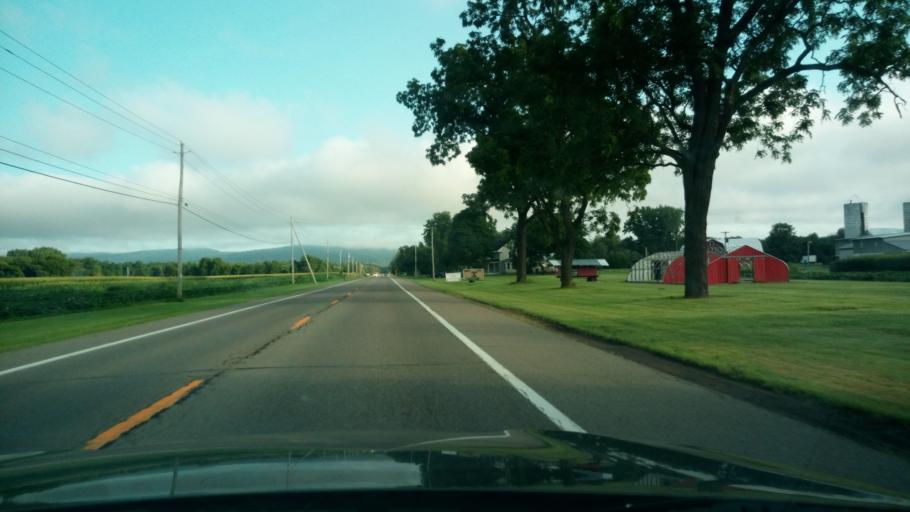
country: US
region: New York
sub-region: Chemung County
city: Big Flats
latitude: 42.1183
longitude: -76.9262
